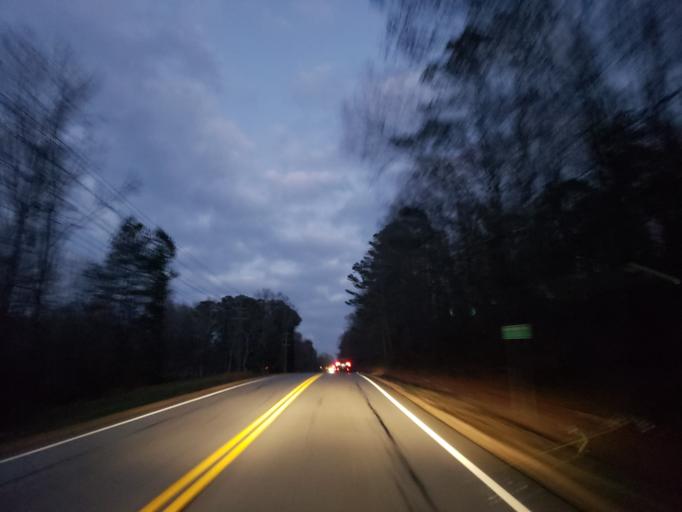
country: US
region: Georgia
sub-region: Carroll County
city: Temple
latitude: 33.8413
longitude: -84.9886
